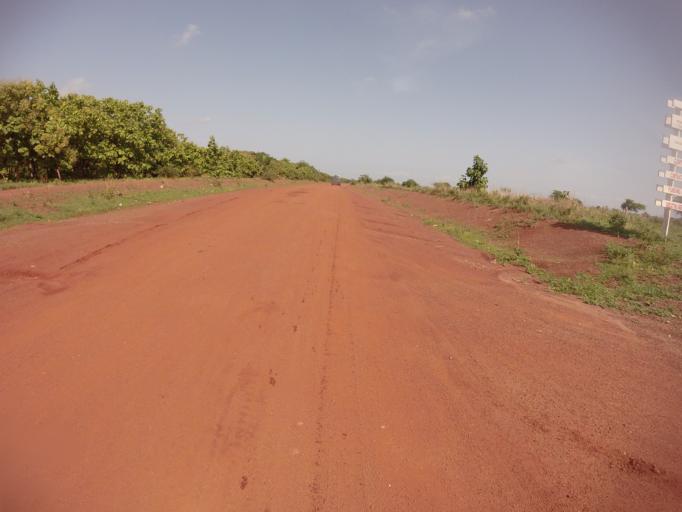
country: GH
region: Upper East
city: Bawku
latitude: 11.0019
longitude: -0.1966
